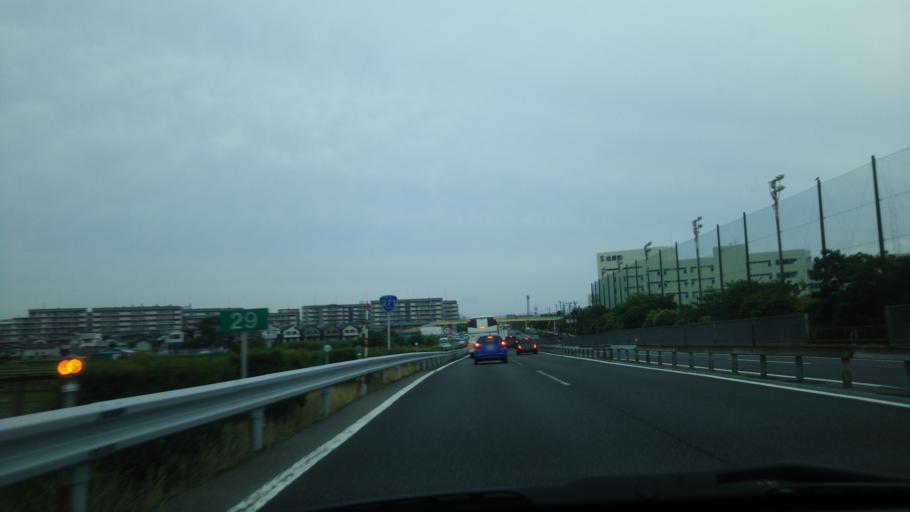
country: JP
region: Kanagawa
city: Isehara
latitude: 35.4053
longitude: 139.3377
